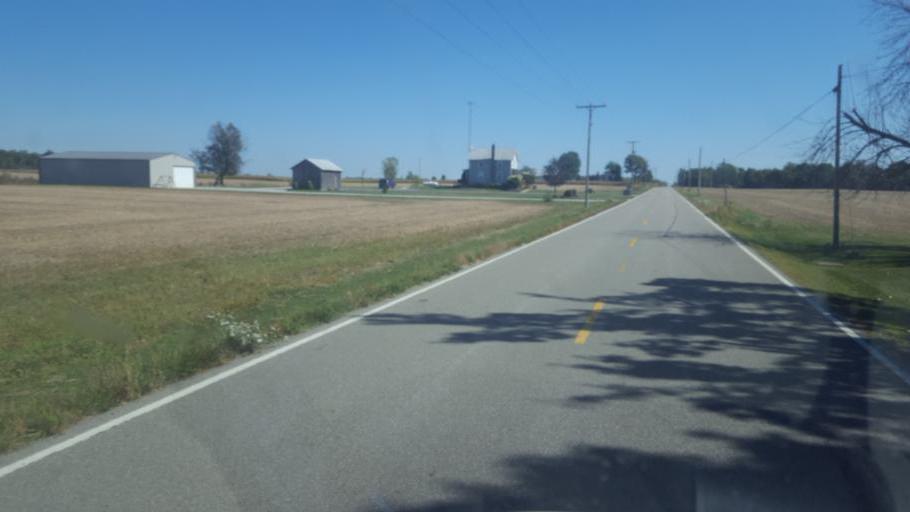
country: US
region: Ohio
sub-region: Crawford County
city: Bucyrus
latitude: 40.8630
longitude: -83.0866
